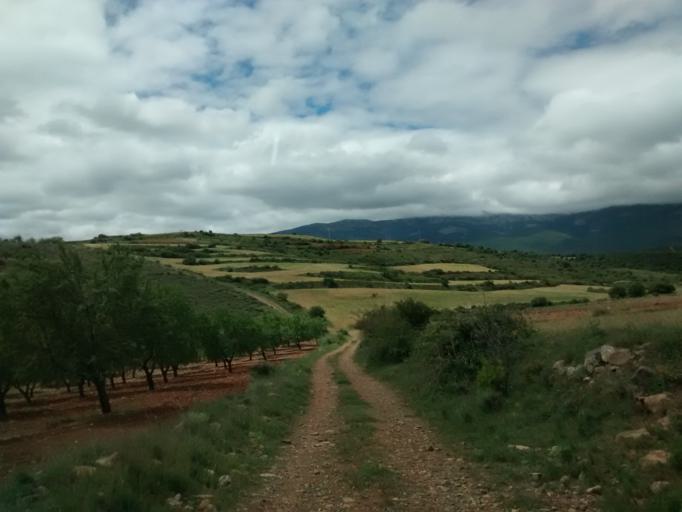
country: ES
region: Aragon
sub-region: Provincia de Zaragoza
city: Trasmoz
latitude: 41.8336
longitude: -1.7411
